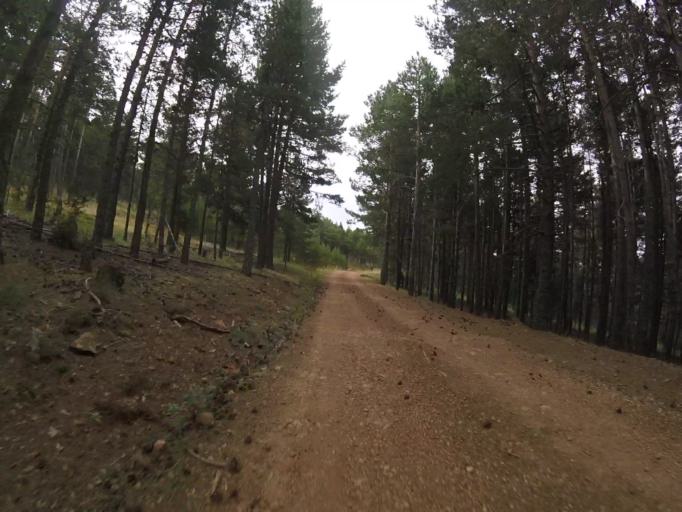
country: ES
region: Aragon
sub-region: Provincia de Teruel
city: Valdelinares
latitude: 40.3555
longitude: -0.5983
